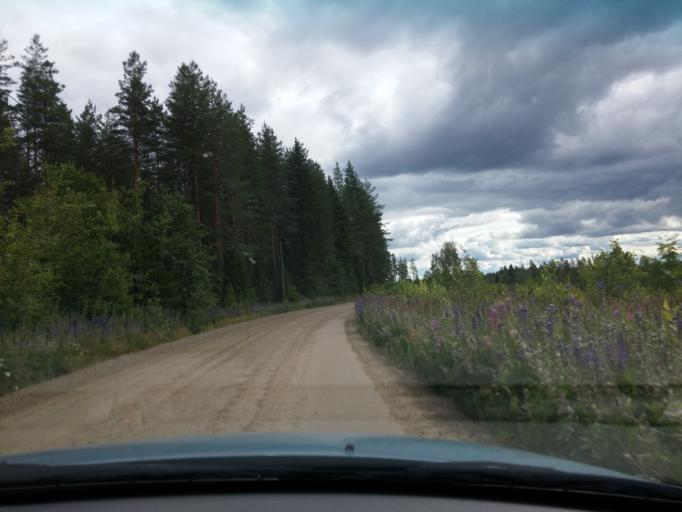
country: FI
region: Central Finland
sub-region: AEaenekoski
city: AEaenekoski
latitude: 62.7588
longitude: 25.6043
